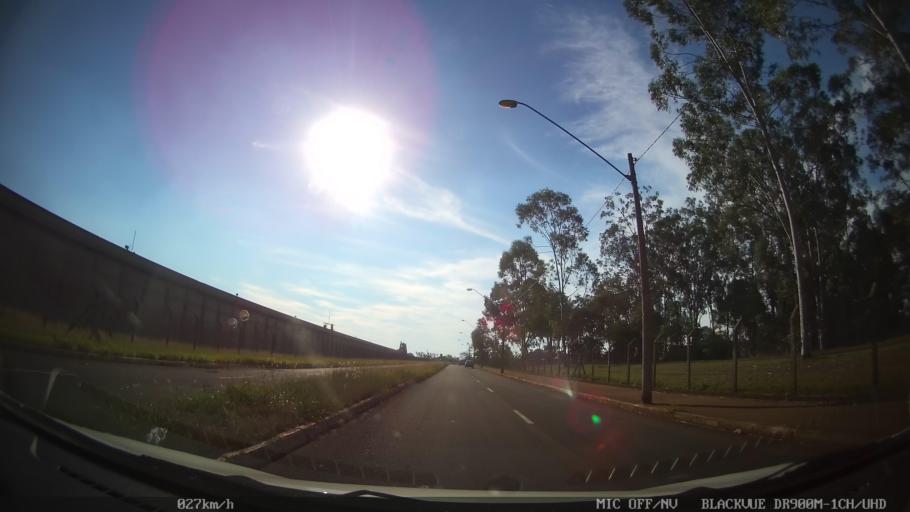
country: BR
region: Sao Paulo
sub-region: Araraquara
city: Araraquara
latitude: -21.7639
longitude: -48.1348
